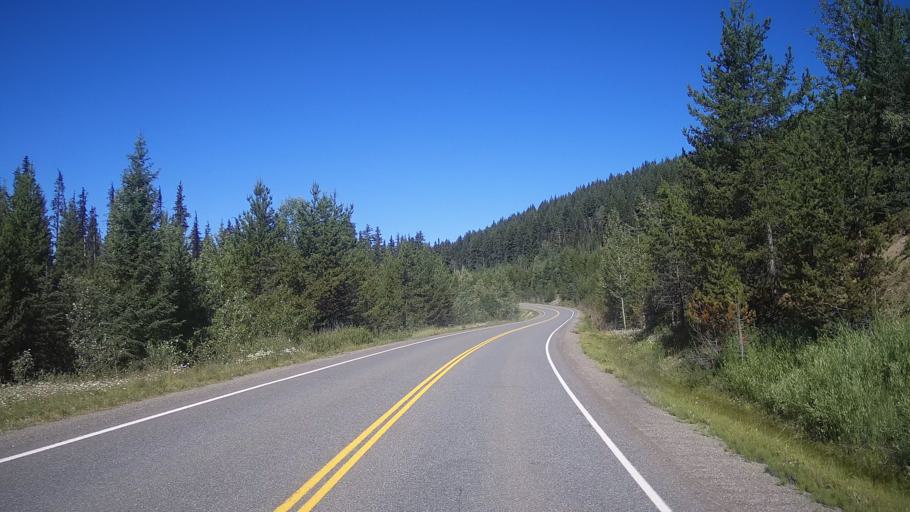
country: CA
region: British Columbia
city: Kamloops
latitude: 51.4958
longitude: -120.4169
